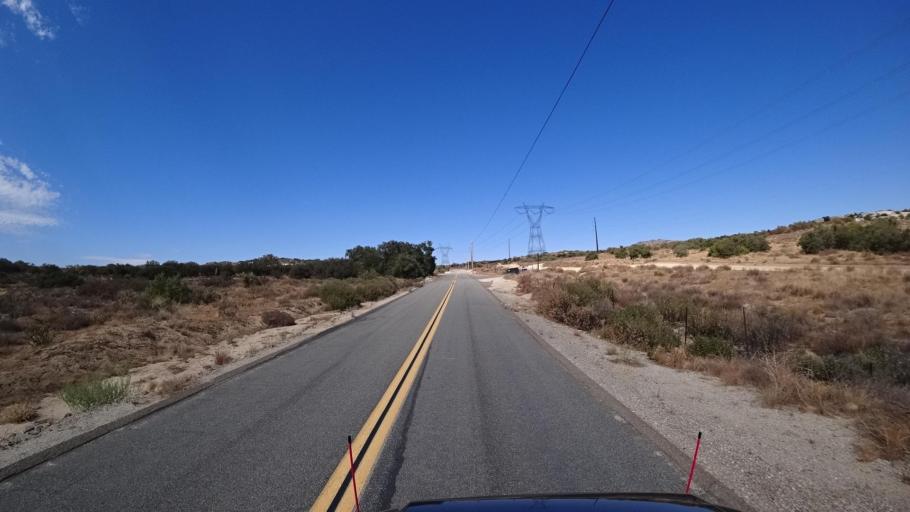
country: MX
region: Baja California
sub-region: Tecate
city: Cereso del Hongo
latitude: 32.6727
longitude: -116.2592
